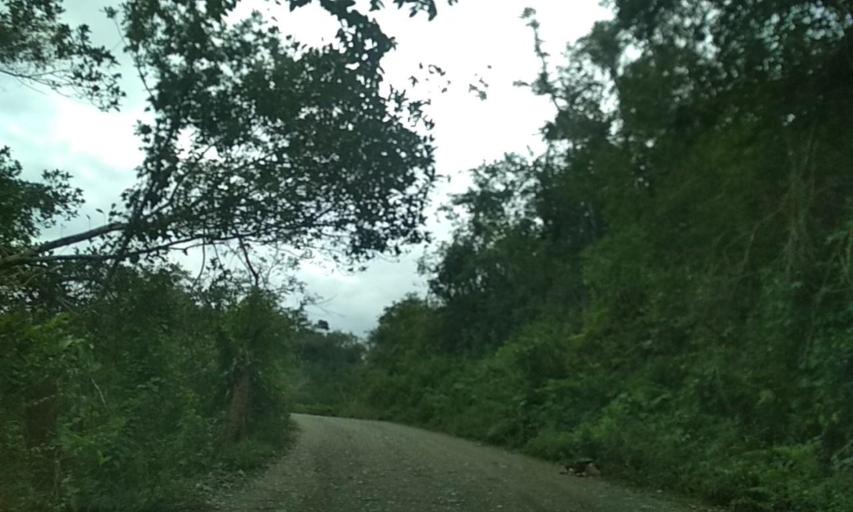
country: MX
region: Veracruz
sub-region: Papantla
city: Residencial Tajin
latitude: 20.6205
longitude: -97.3614
